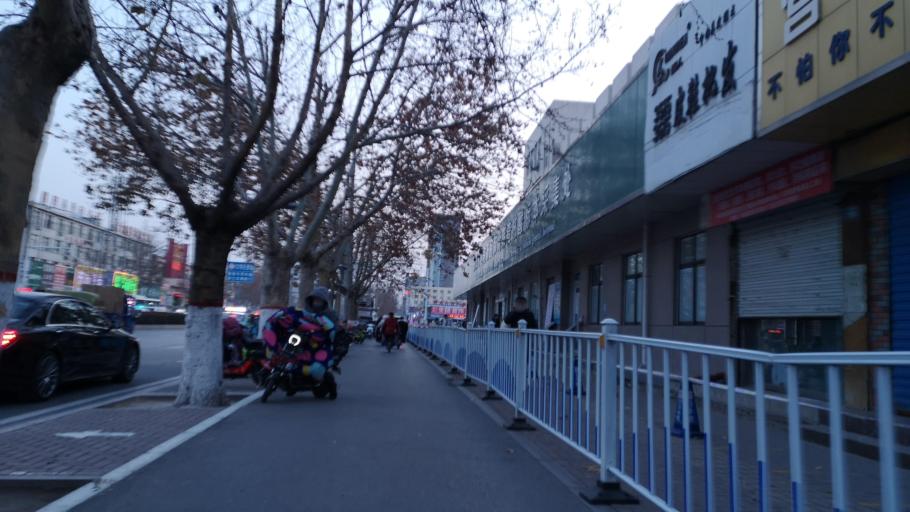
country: CN
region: Henan Sheng
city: Zhongyuanlu
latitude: 35.7718
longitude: 115.0695
